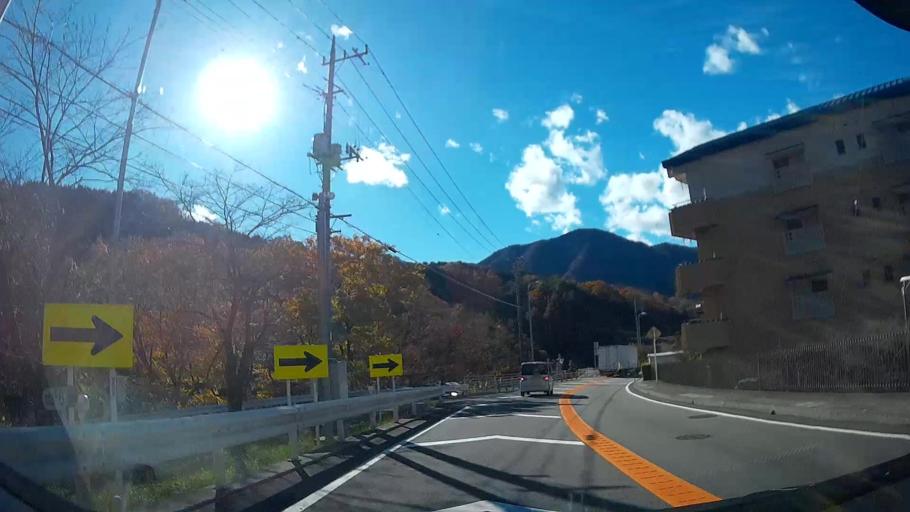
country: JP
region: Yamanashi
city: Enzan
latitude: 35.6388
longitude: 138.7821
